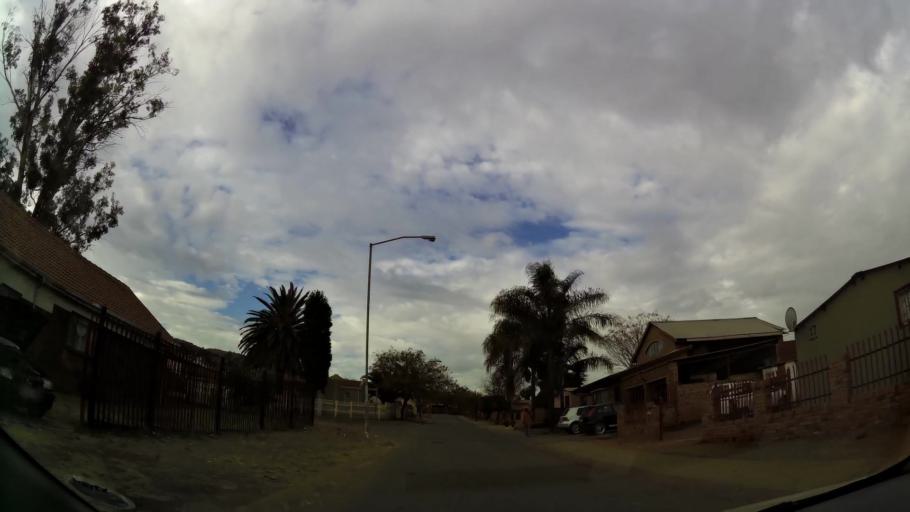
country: ZA
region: Gauteng
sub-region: City of Tshwane Metropolitan Municipality
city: Pretoria
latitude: -25.6992
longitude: 28.2991
